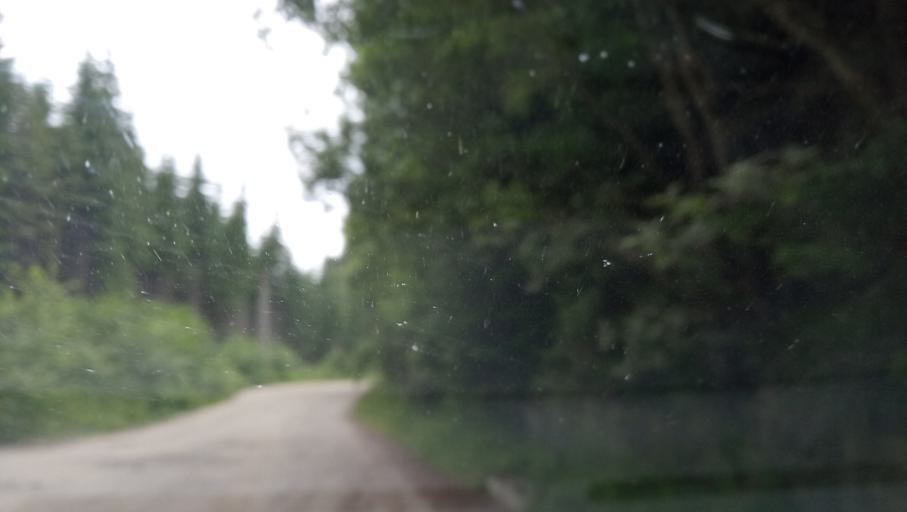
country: RO
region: Valcea
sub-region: Comuna Voineasa
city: Voineasa
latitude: 45.4268
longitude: 23.7561
